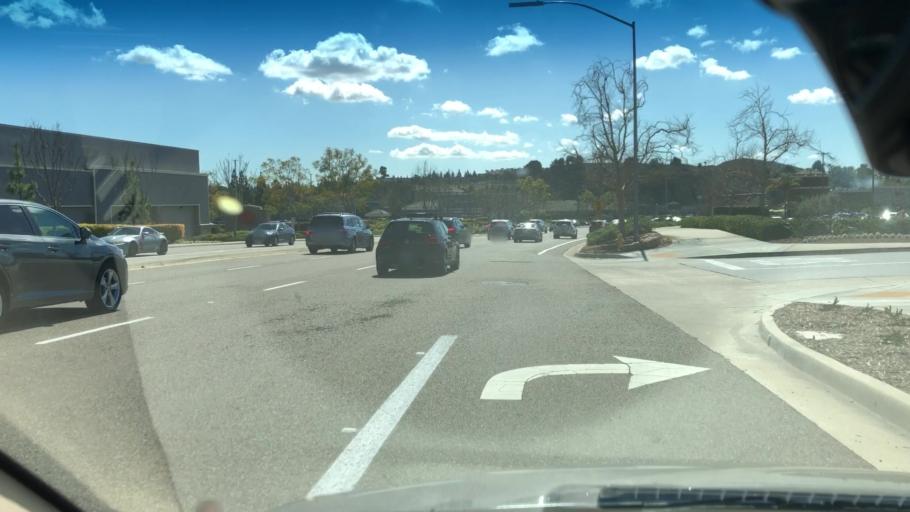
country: US
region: California
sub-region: San Diego County
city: Poway
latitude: 32.9852
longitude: -117.0757
